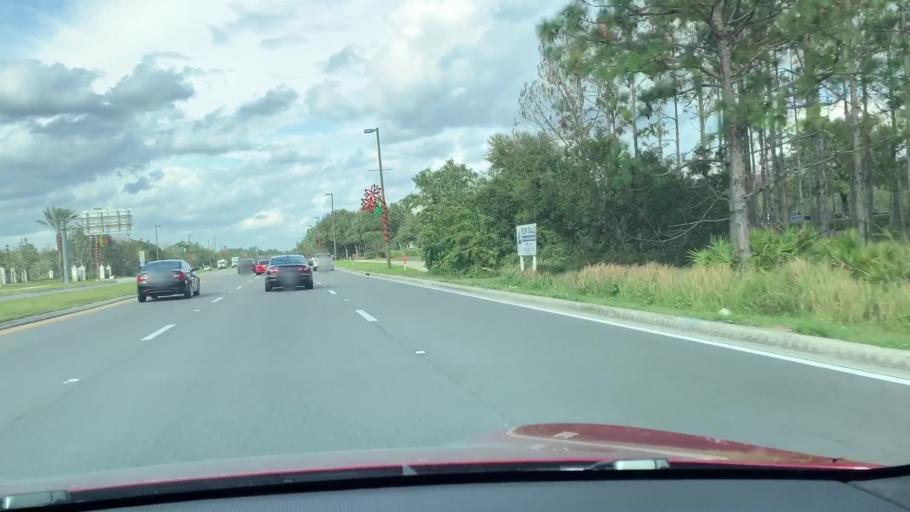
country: US
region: Florida
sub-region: Osceola County
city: Celebration
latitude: 28.3618
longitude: -81.4870
